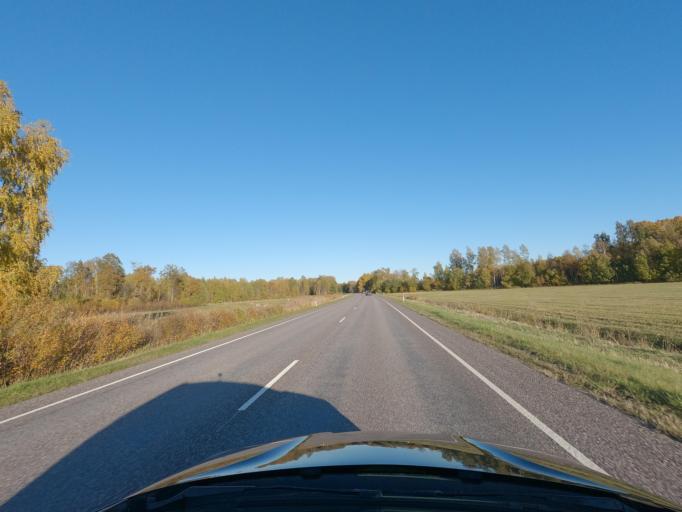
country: EE
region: Saare
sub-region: Orissaare vald
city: Orissaare
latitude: 58.5258
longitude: 23.0546
